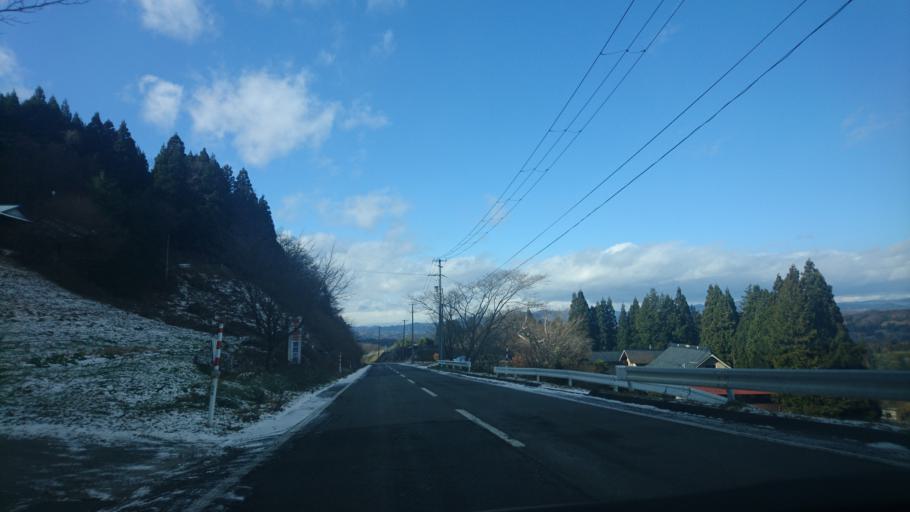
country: JP
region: Iwate
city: Ichinoseki
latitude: 38.9738
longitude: 141.3941
